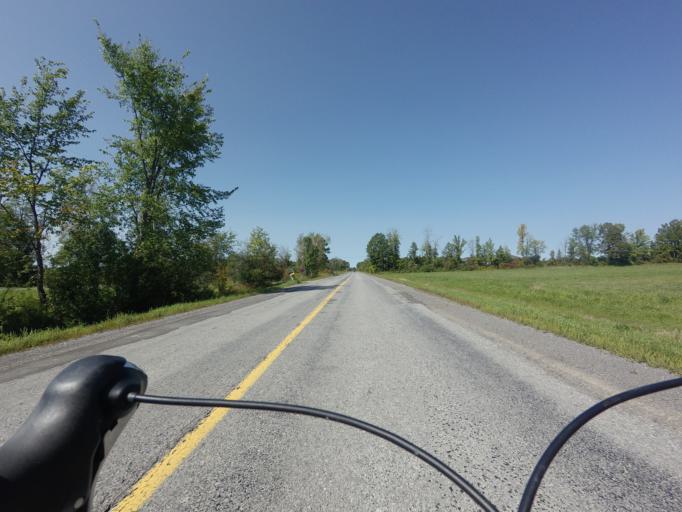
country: CA
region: Ontario
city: Bells Corners
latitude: 45.4291
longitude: -76.0552
